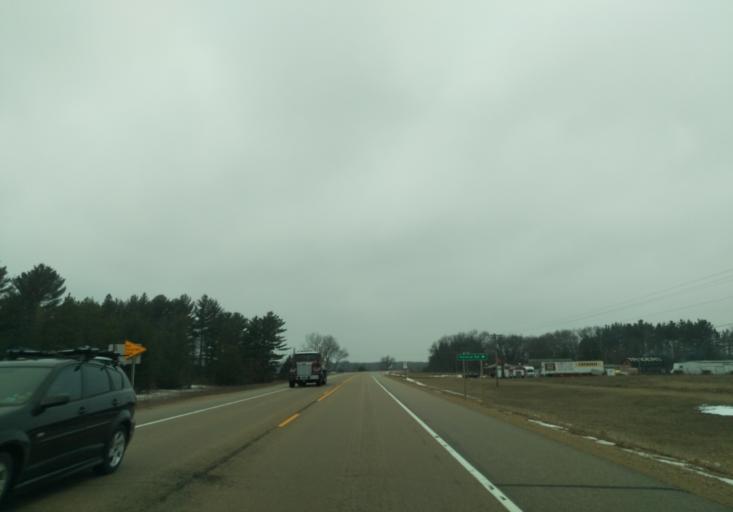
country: US
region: Wisconsin
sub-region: Sauk County
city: Spring Green
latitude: 43.1616
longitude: -90.0207
